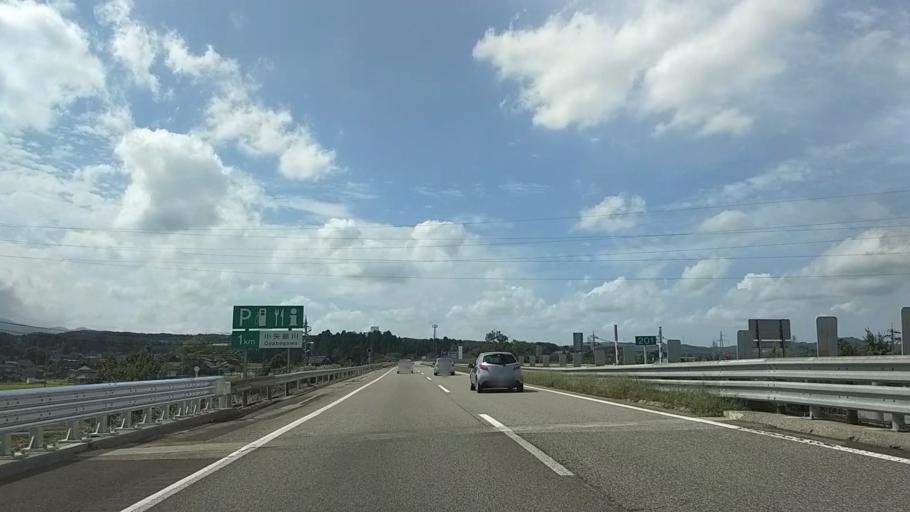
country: JP
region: Toyama
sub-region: Oyabe Shi
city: Oyabe
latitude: 36.6303
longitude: 136.8859
